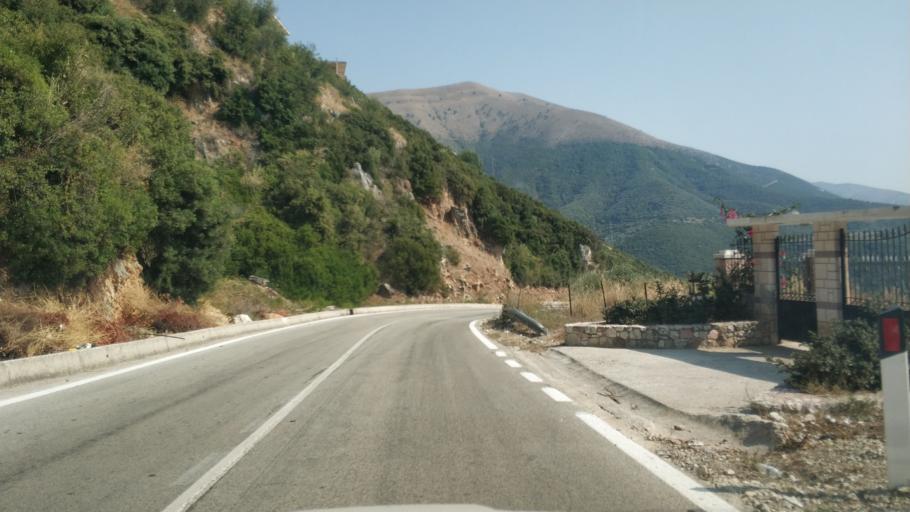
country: AL
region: Vlore
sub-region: Rrethi i Sarandes
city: Lukove
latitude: 40.0151
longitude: 19.8968
